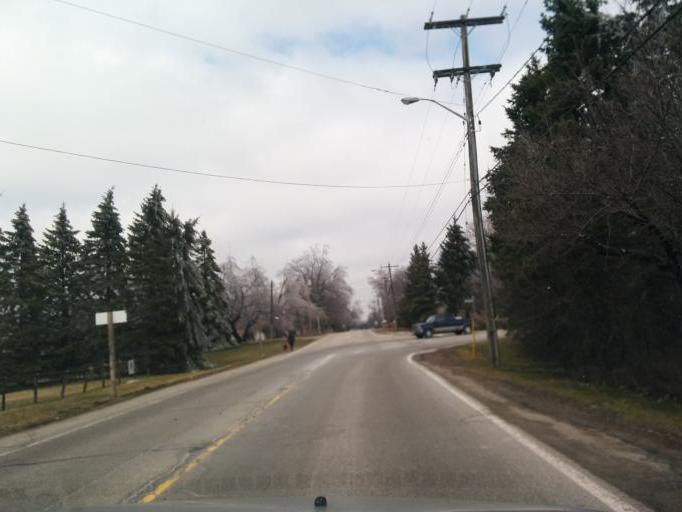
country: CA
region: Ontario
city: Waterloo
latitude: 43.5447
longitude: -80.5537
